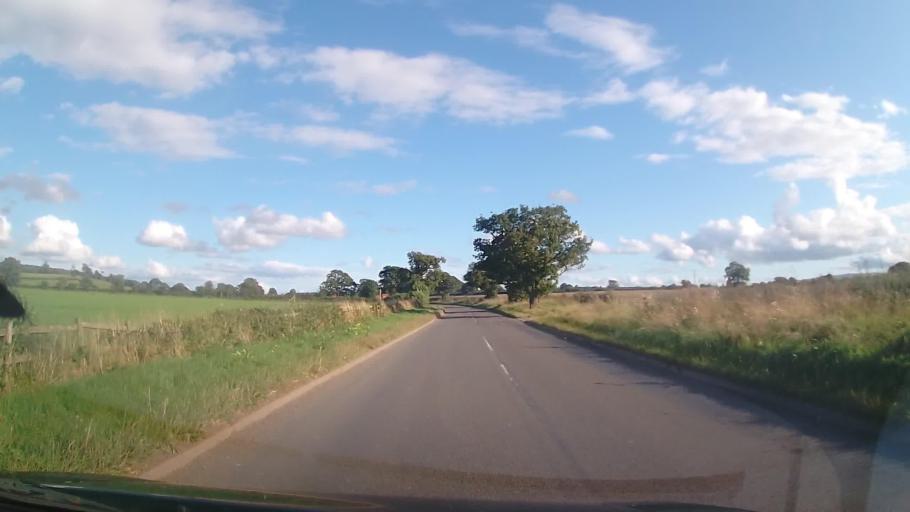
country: GB
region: England
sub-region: Shropshire
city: Great Hanwood
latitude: 52.6575
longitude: -2.8104
